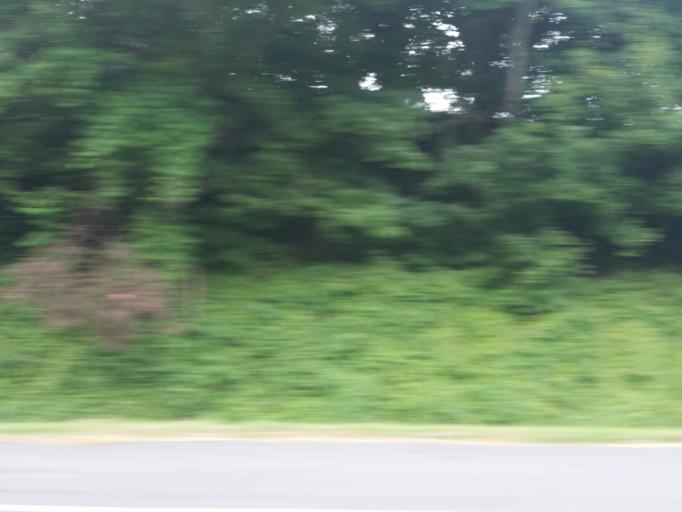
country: US
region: Kentucky
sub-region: Ballard County
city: Wickliffe
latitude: 36.9706
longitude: -89.0936
